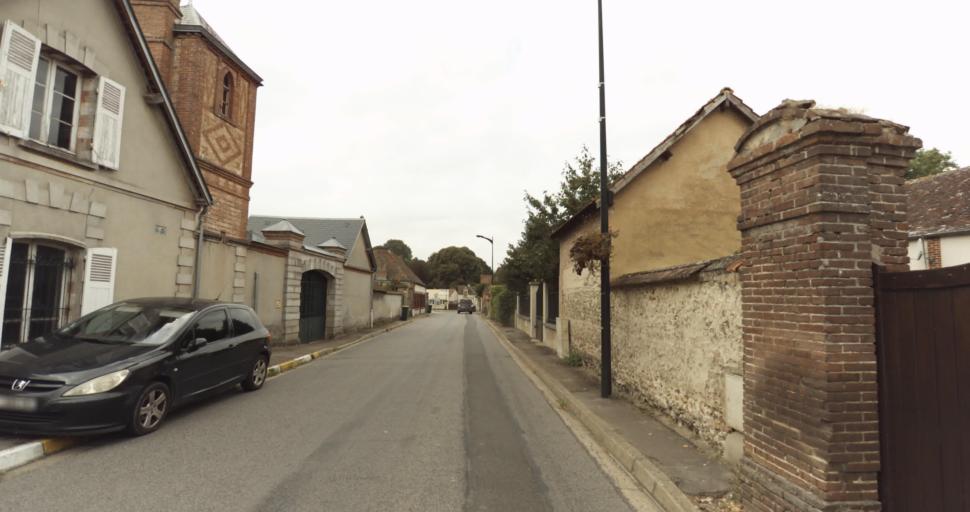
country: FR
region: Haute-Normandie
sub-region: Departement de l'Eure
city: Marcilly-sur-Eure
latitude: 48.8264
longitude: 1.3477
